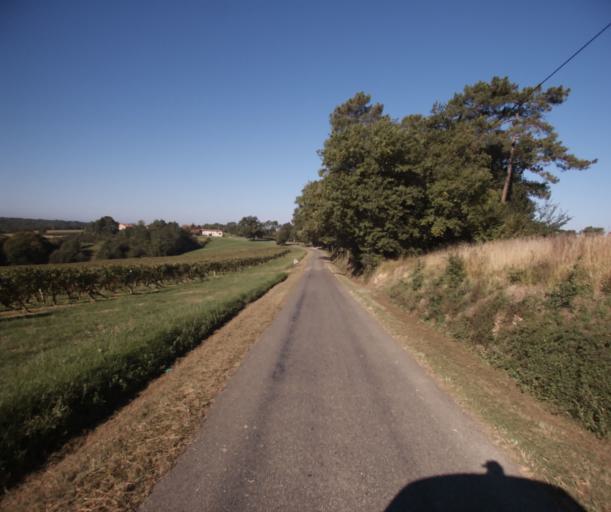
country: FR
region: Aquitaine
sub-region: Departement des Landes
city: Gabarret
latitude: 43.9065
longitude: 0.0230
